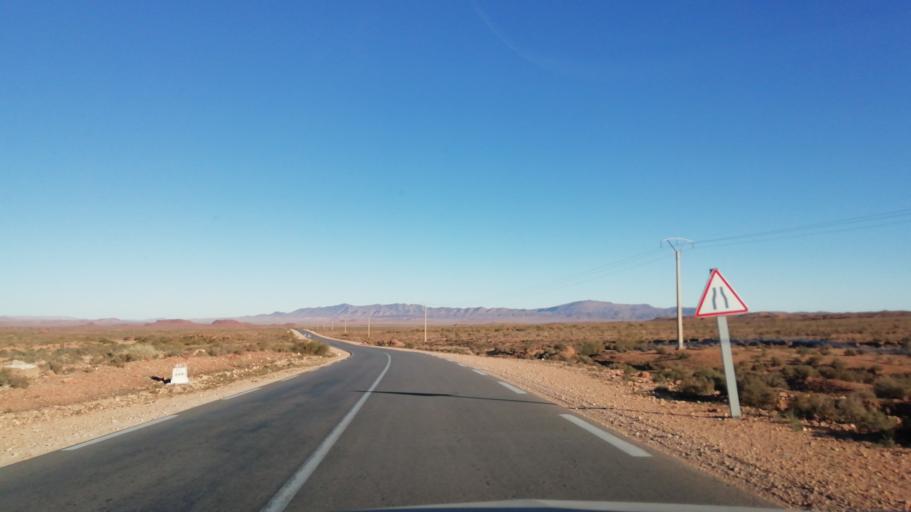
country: DZ
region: El Bayadh
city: El Abiodh Sidi Cheikh
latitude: 33.1668
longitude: 0.4656
